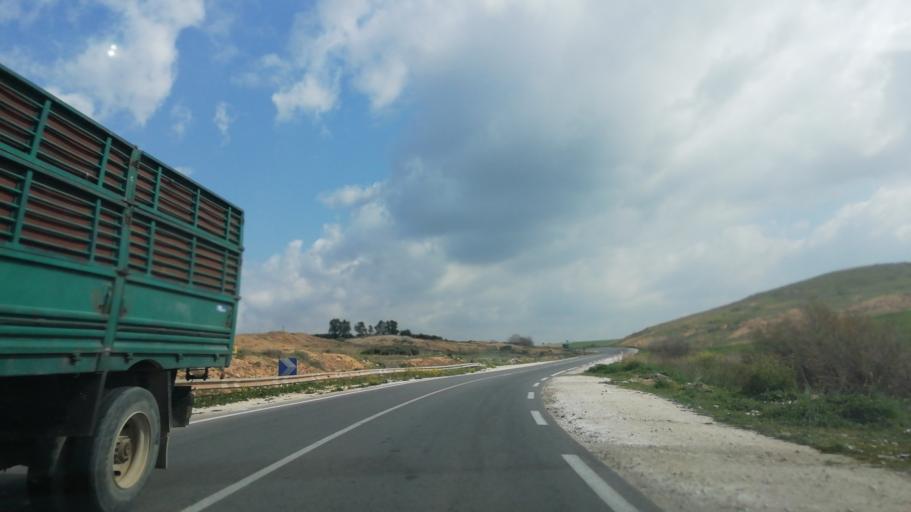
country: DZ
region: Mostaganem
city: Mostaganem
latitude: 35.7010
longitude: 0.2418
